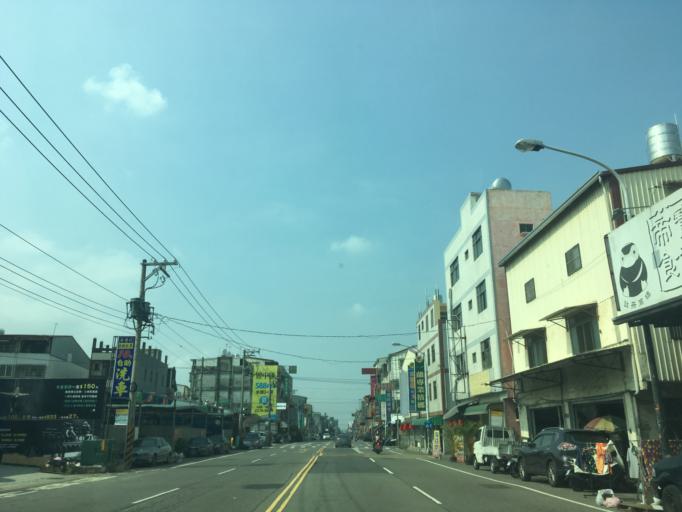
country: TW
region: Taiwan
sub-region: Taichung City
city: Taichung
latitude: 24.1566
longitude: 120.7123
